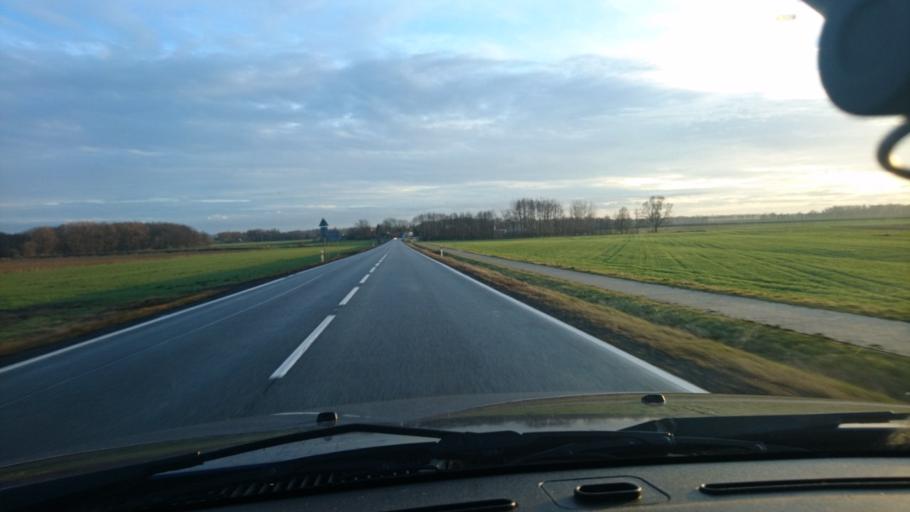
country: PL
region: Greater Poland Voivodeship
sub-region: Powiat kepinski
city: Opatow
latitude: 51.1742
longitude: 18.1450
